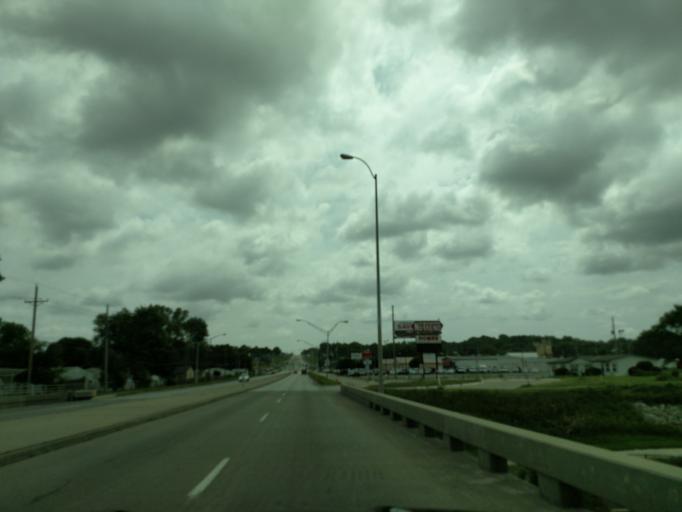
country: US
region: Nebraska
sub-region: Douglas County
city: Ralston
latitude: 41.2124
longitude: -96.0121
